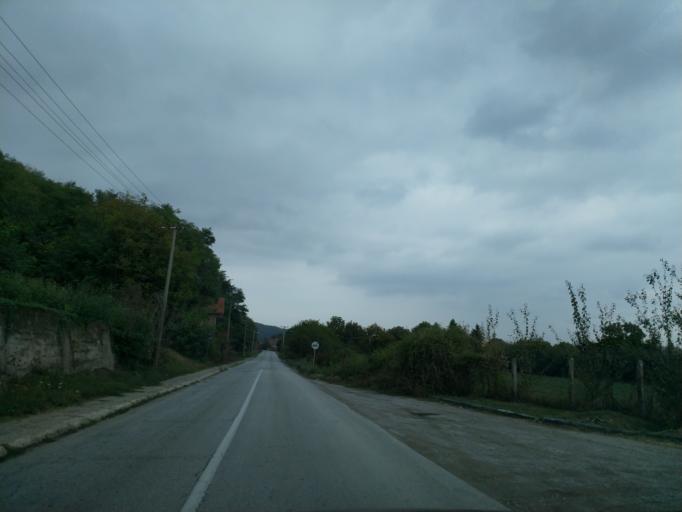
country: RS
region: Central Serbia
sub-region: Sumadijski Okrug
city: Batocina
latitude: 44.0811
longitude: 21.1812
